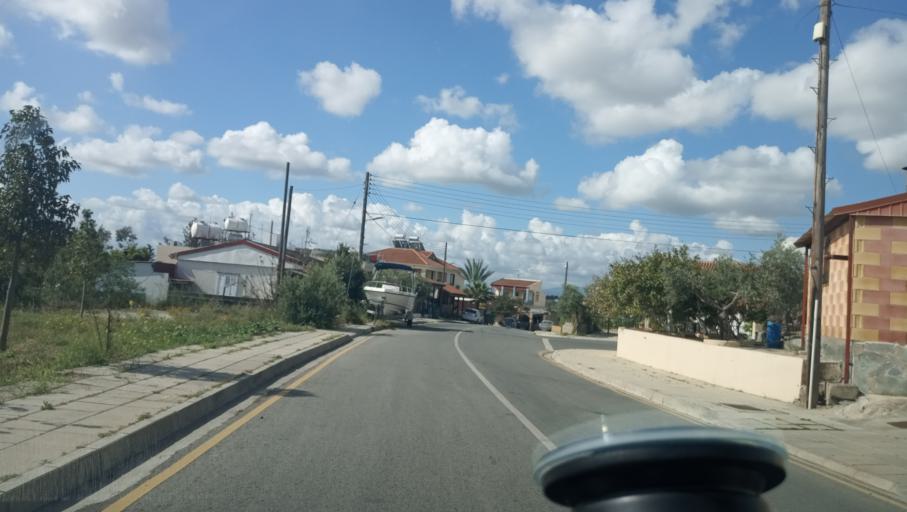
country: CY
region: Lefkosia
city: Geri
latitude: 35.1002
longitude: 33.4080
